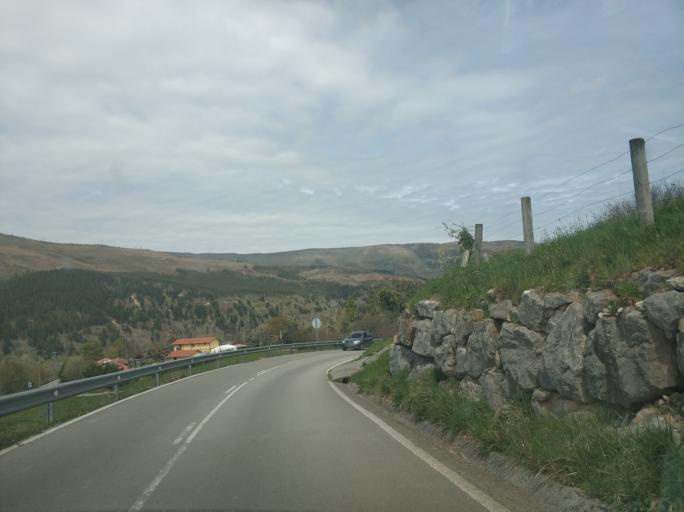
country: ES
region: Cantabria
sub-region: Provincia de Cantabria
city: Ruente
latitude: 43.2370
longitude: -4.2821
